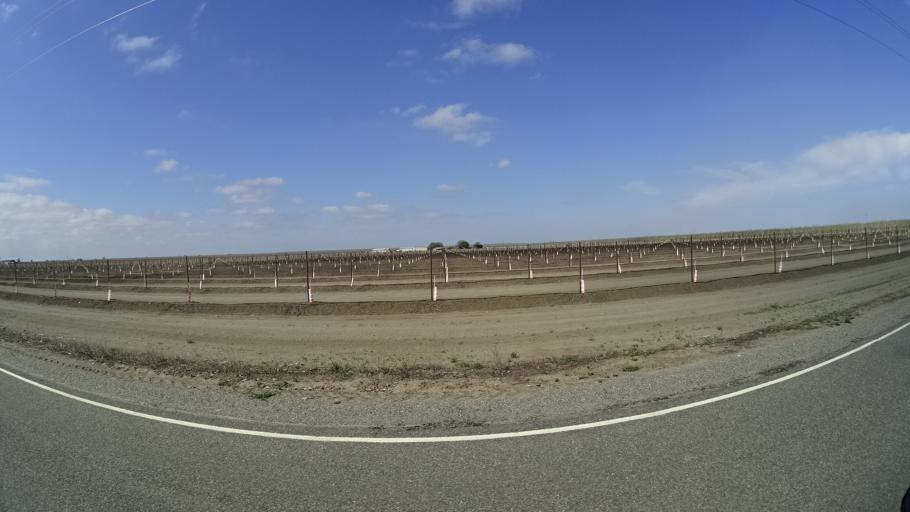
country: US
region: California
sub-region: Butte County
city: Biggs
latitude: 39.4401
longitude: -121.9298
